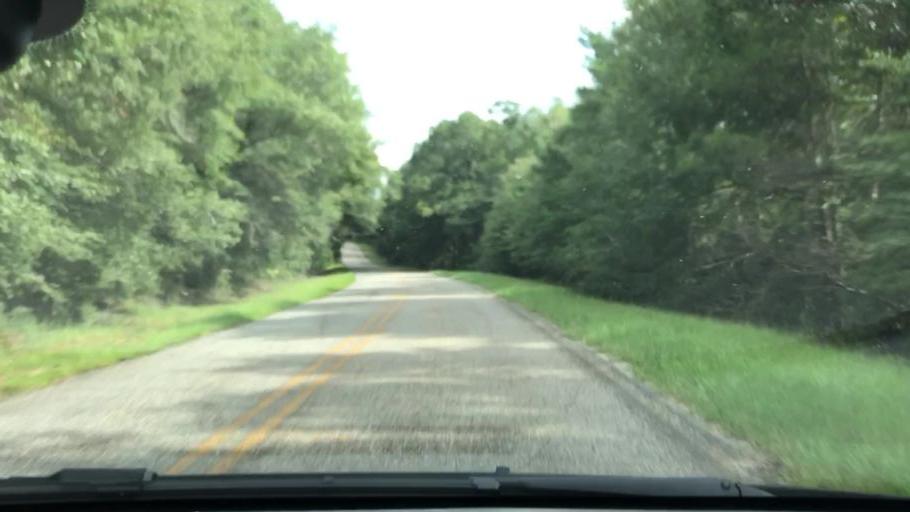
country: US
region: Georgia
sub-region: Early County
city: Blakely
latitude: 31.5089
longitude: -84.9509
